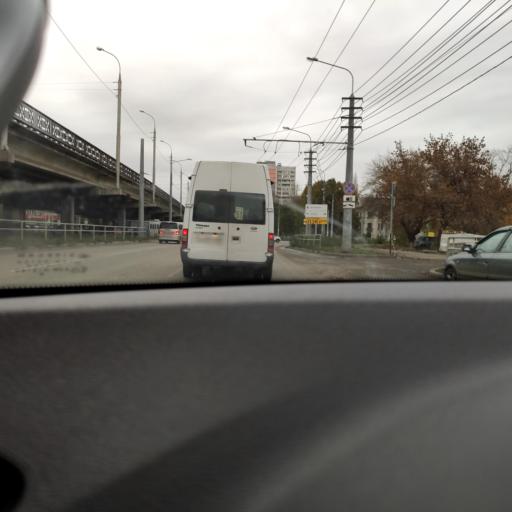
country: RU
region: Samara
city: Smyshlyayevka
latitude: 53.2066
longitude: 50.2756
